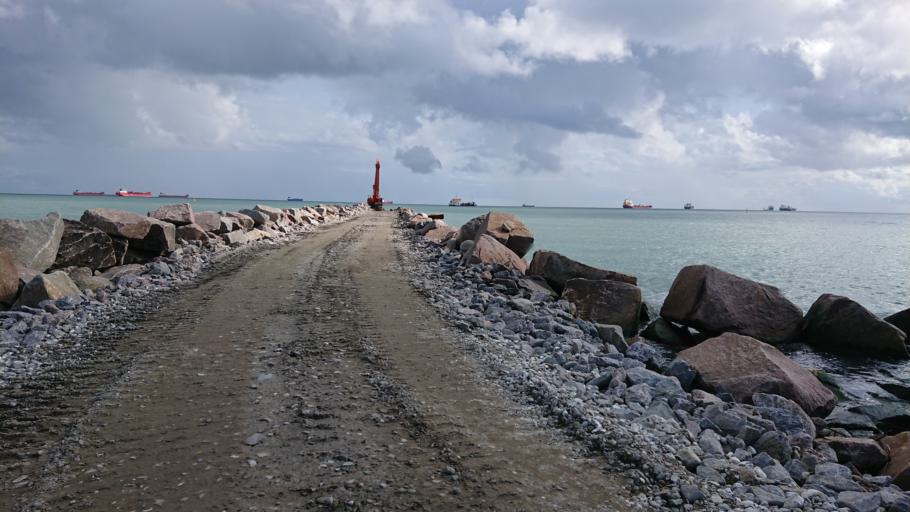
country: DK
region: North Denmark
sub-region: Frederikshavn Kommune
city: Skagen
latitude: 57.7207
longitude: 10.6067
